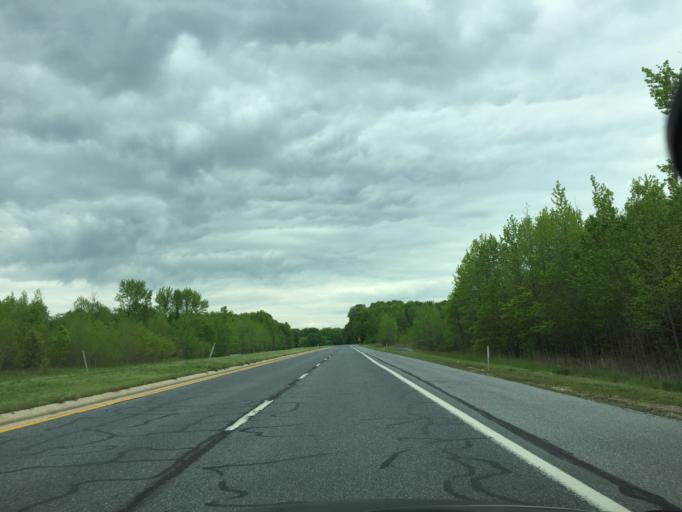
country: US
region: Maryland
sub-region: Baltimore County
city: Middle River
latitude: 39.2963
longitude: -76.4368
